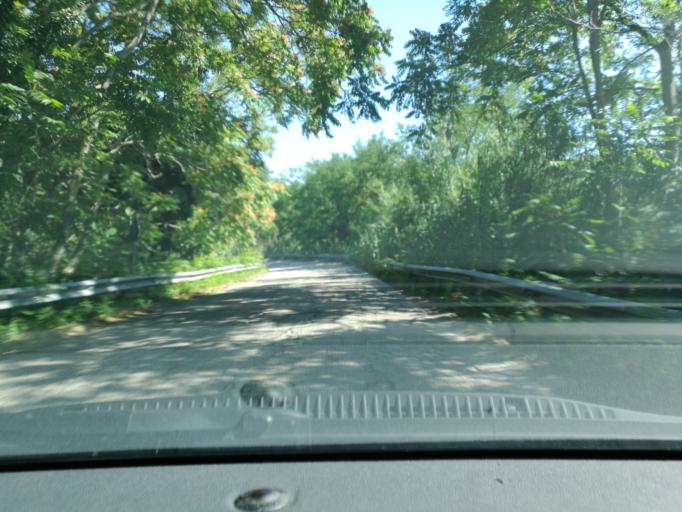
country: IT
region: Abruzzo
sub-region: Provincia di Chieti
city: Vasto
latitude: 42.1654
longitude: 14.6988
